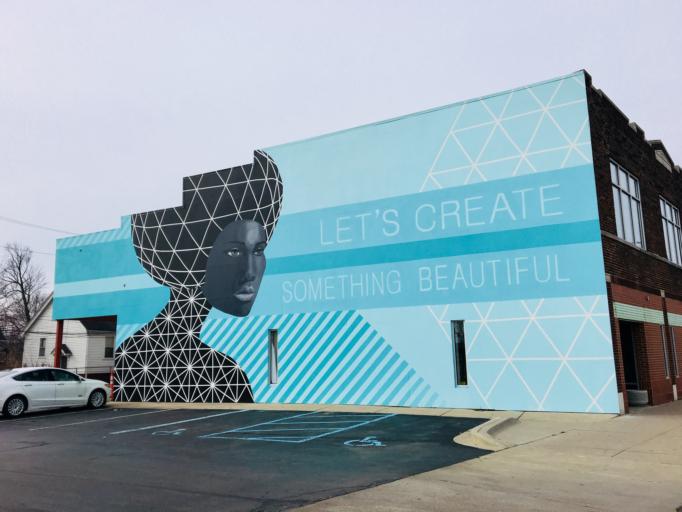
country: US
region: Michigan
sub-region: Wayne County
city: Grosse Pointe Park
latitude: 42.3868
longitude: -82.9501
